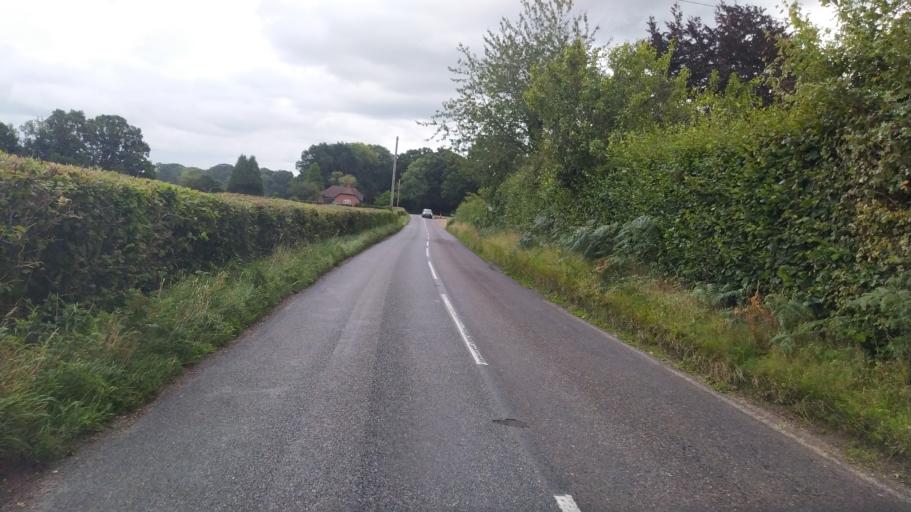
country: GB
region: England
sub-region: Dorset
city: Verwood
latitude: 50.9107
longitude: -1.8846
